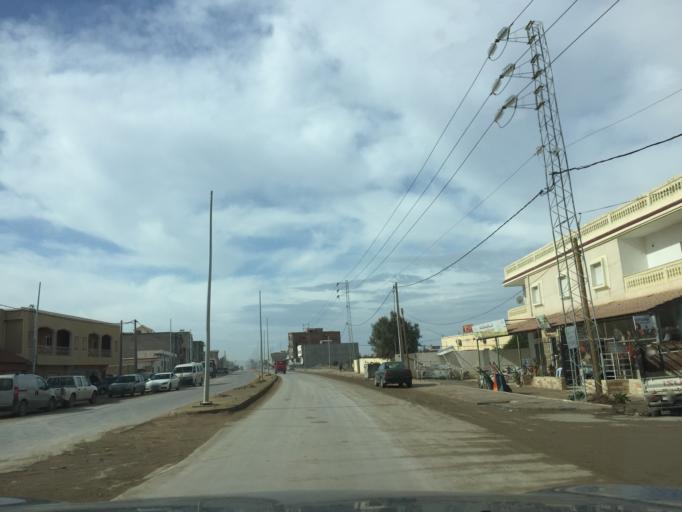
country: TN
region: Zaghwan
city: El Fahs
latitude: 36.3690
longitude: 9.8975
